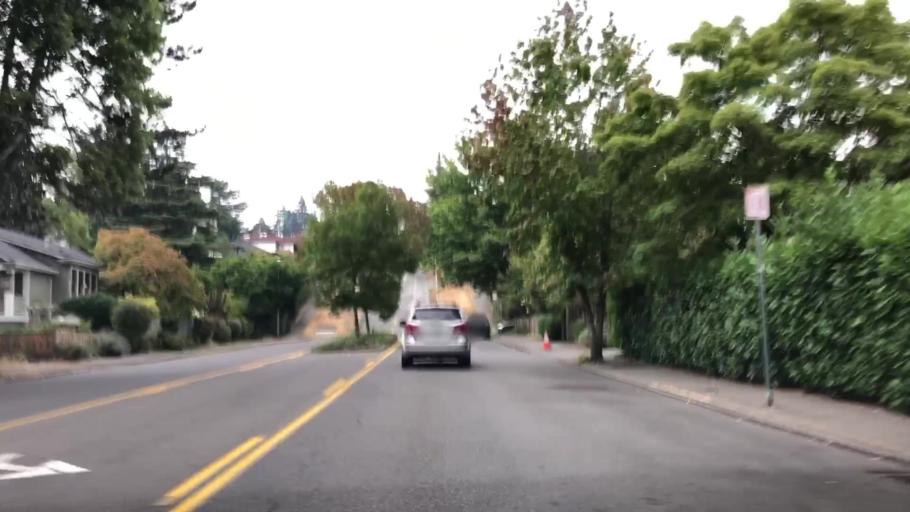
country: US
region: Washington
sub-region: King County
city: Medina
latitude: 47.6584
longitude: -122.2838
